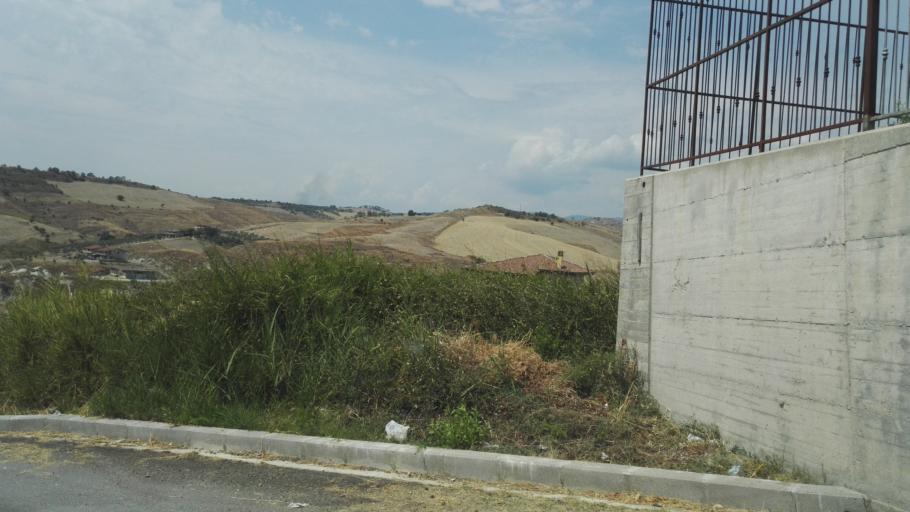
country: IT
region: Calabria
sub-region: Provincia di Reggio Calabria
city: Riace Marina
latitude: 38.3923
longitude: 16.5250
